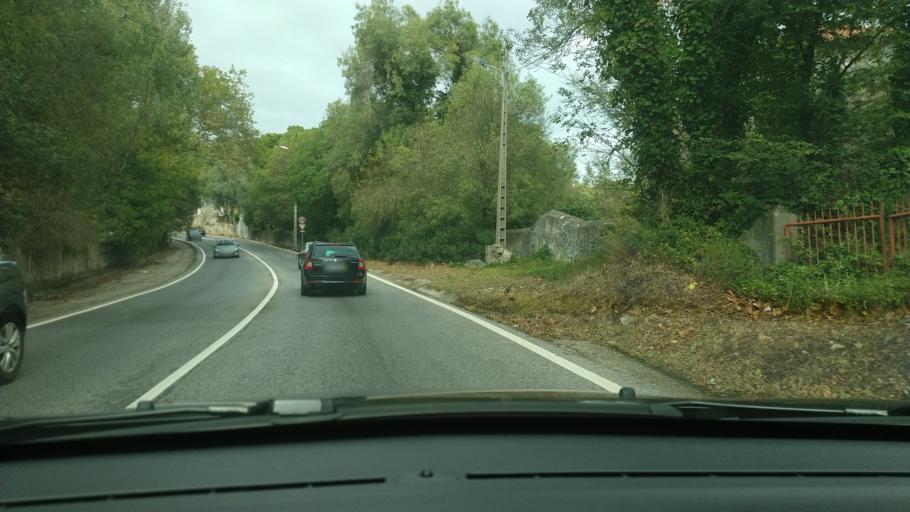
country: PT
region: Lisbon
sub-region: Sintra
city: Sintra
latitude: 38.7856
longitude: -9.3711
